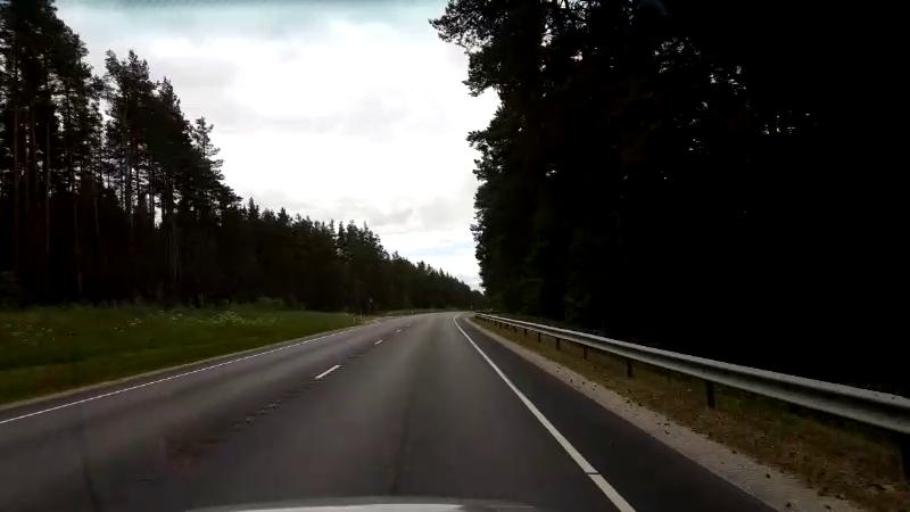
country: EE
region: Paernumaa
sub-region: Paernu linn
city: Parnu
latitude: 58.1616
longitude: 24.4979
